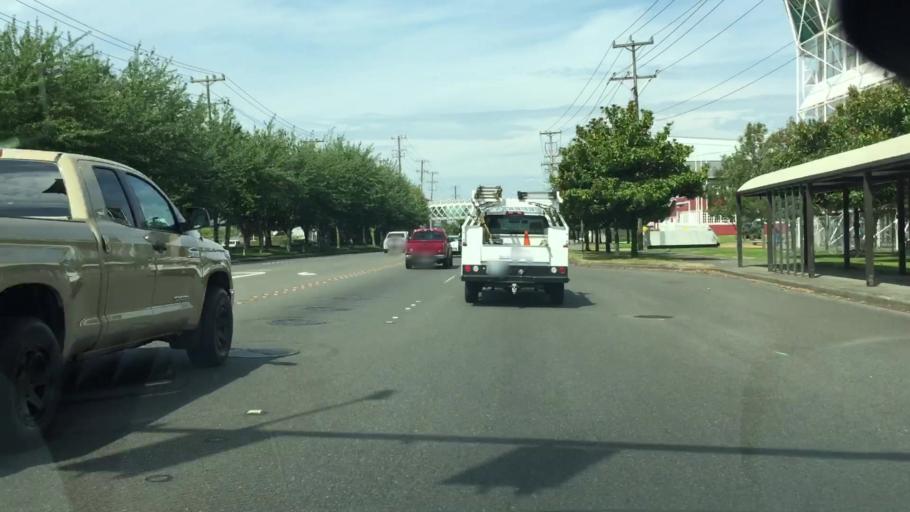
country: US
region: Washington
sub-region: King County
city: Riverton
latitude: 47.5172
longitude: -122.2969
